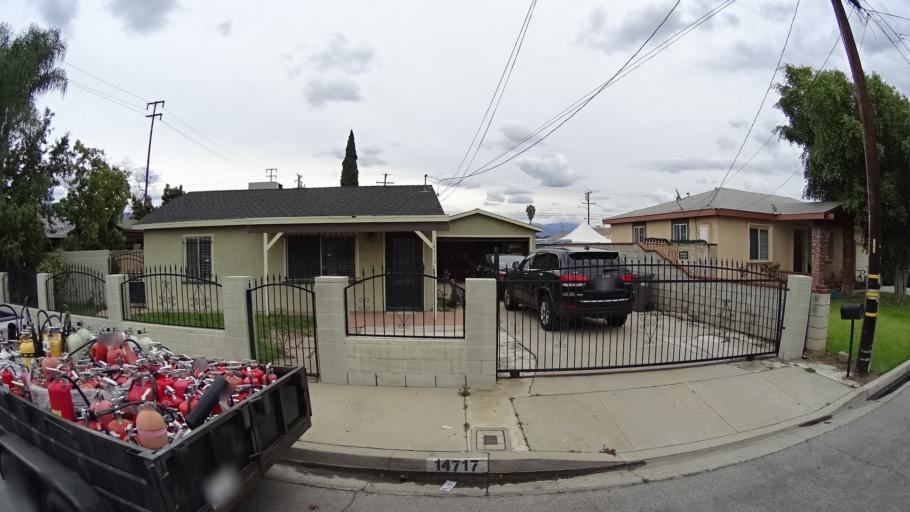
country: US
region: California
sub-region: Los Angeles County
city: Baldwin Park
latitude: 34.0809
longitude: -117.9560
